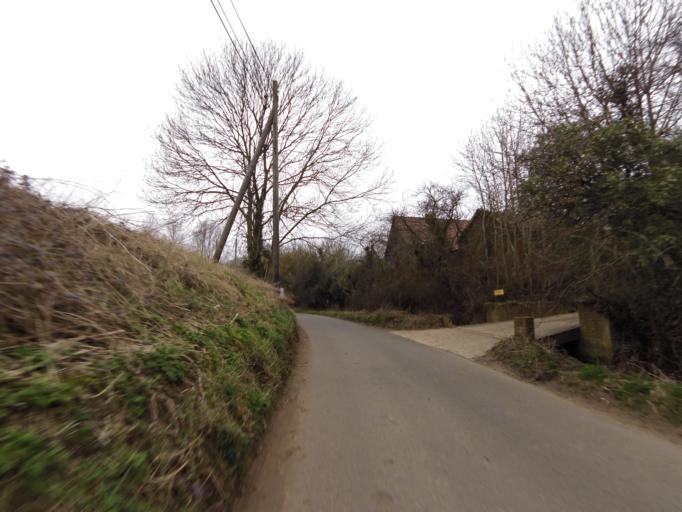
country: GB
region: England
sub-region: Suffolk
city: Framlingham
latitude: 52.2222
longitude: 1.3285
